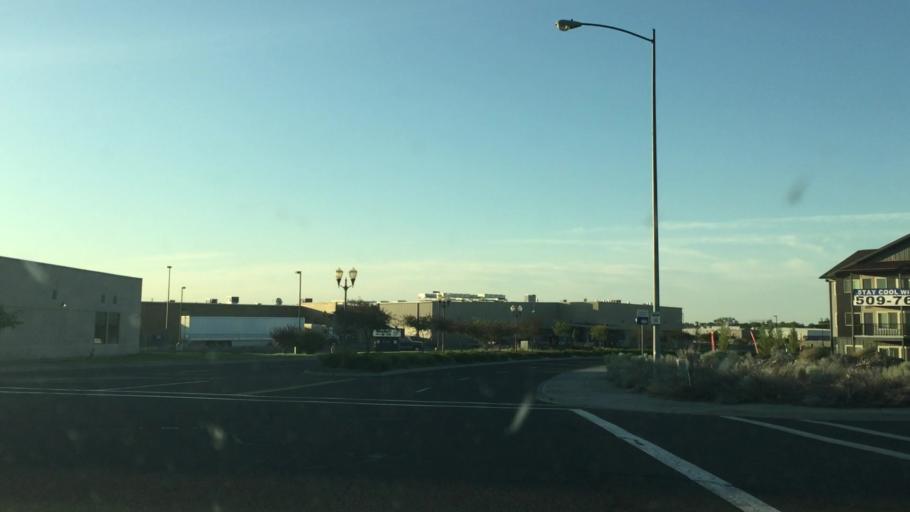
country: US
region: Washington
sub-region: Grant County
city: Moses Lake
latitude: 47.1428
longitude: -119.2842
